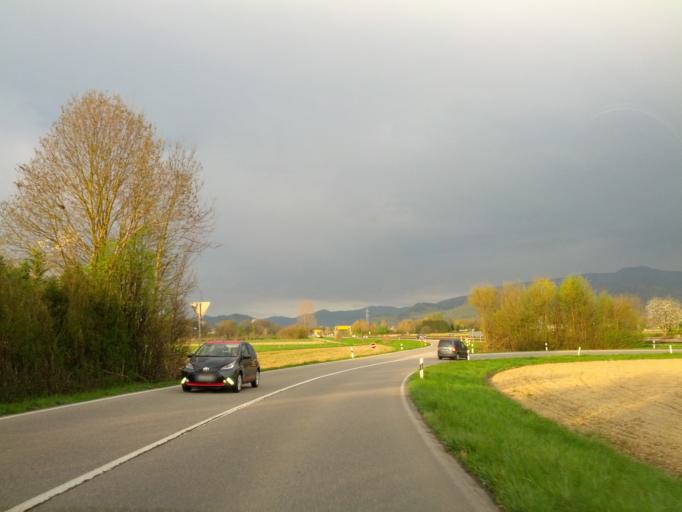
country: DE
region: Baden-Wuerttemberg
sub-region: Freiburg Region
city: Gundelfingen
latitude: 48.0515
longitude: 7.8595
